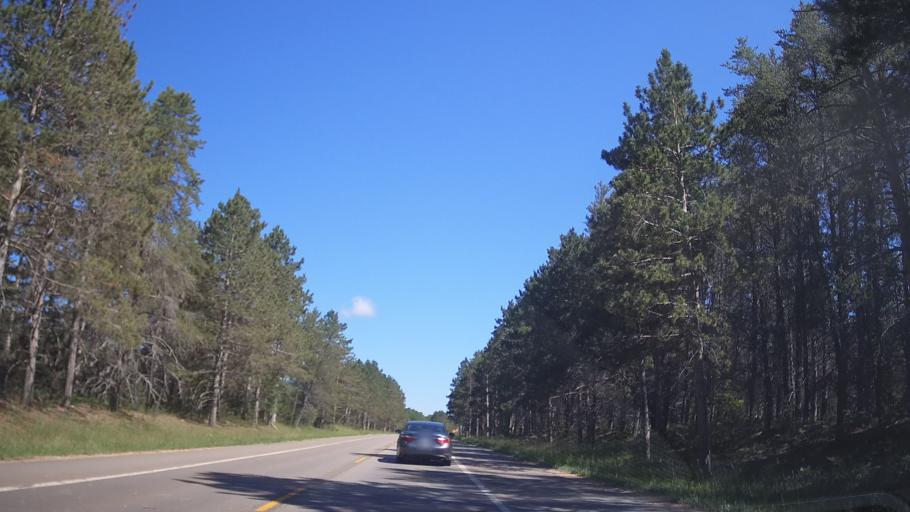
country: US
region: Michigan
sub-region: Cheboygan County
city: Indian River
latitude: 45.5418
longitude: -84.7834
